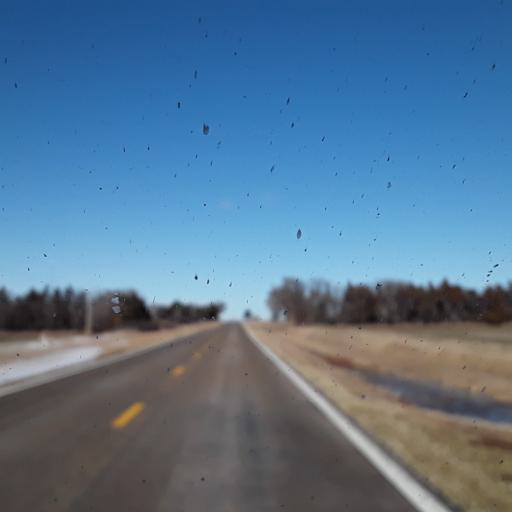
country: US
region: Kansas
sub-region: Mitchell County
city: Beloit
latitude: 39.3408
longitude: -98.1161
